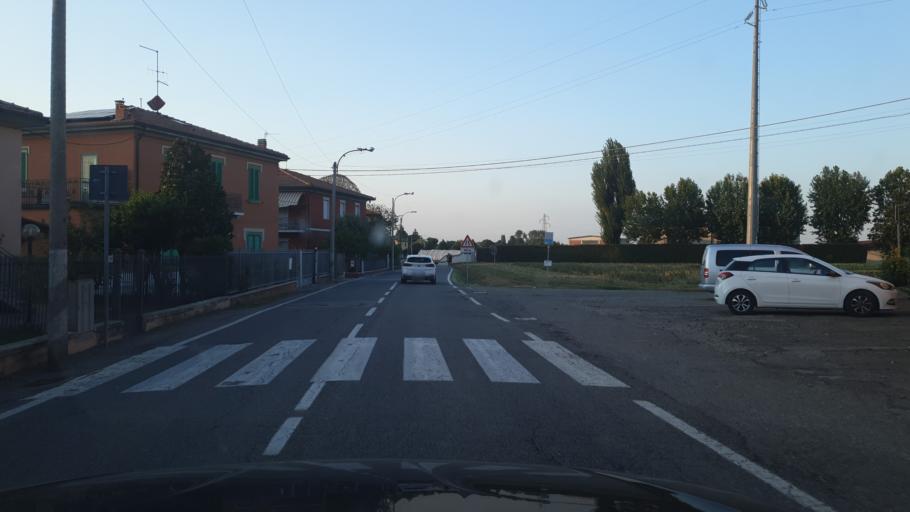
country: IT
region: Emilia-Romagna
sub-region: Provincia di Bologna
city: Quarto Inferiore
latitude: 44.5193
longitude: 11.3811
